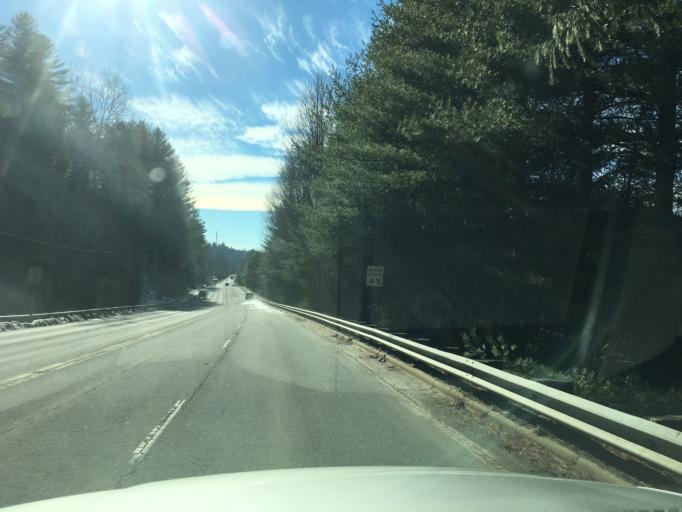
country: US
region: North Carolina
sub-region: Transylvania County
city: Brevard
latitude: 35.2916
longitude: -82.6858
